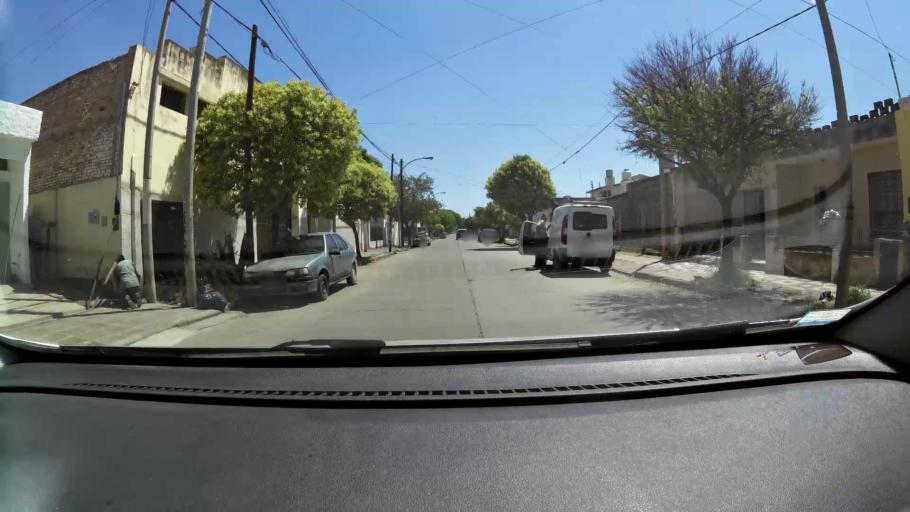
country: AR
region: Cordoba
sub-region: Departamento de Capital
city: Cordoba
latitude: -31.3822
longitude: -64.1504
